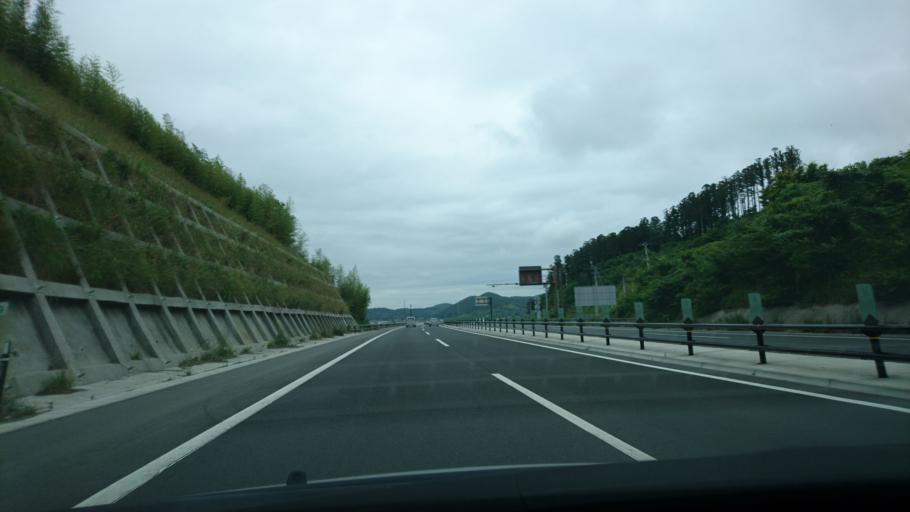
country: JP
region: Miyagi
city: Ishinomaki
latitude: 38.5030
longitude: 141.2862
